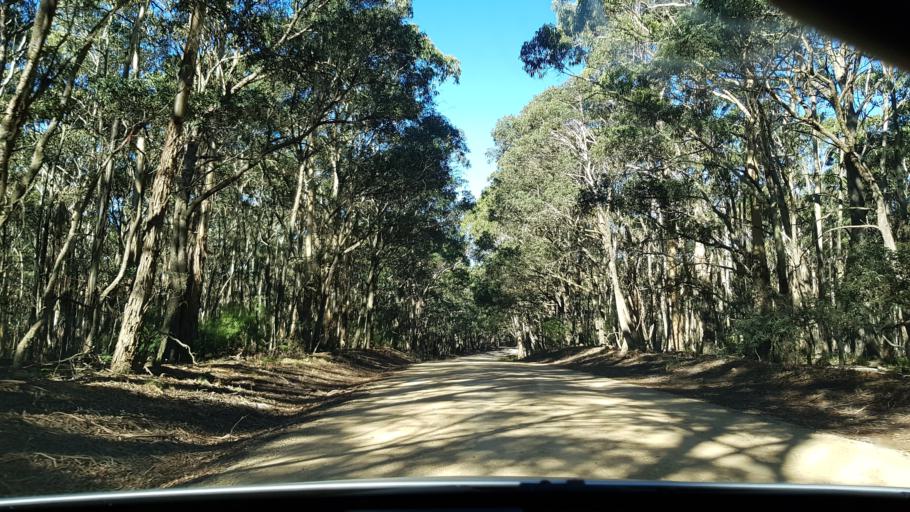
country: AU
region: New South Wales
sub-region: Oberon
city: Oberon
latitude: -33.8521
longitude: 150.0356
